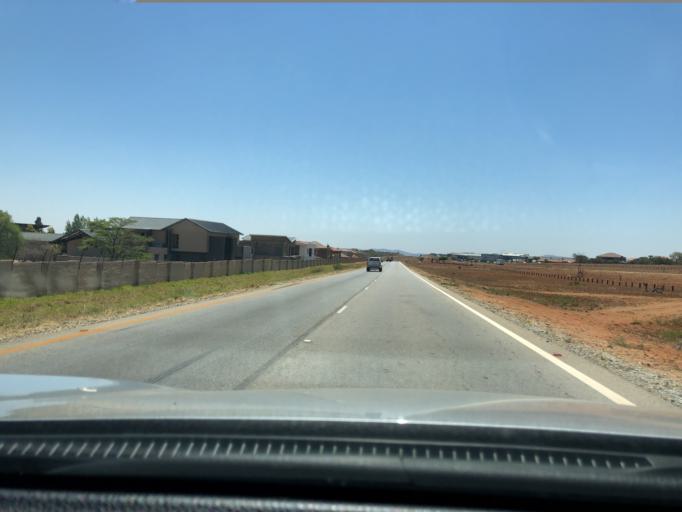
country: ZA
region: Limpopo
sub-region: Capricorn District Municipality
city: Polokwane
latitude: -23.8866
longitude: 29.5078
